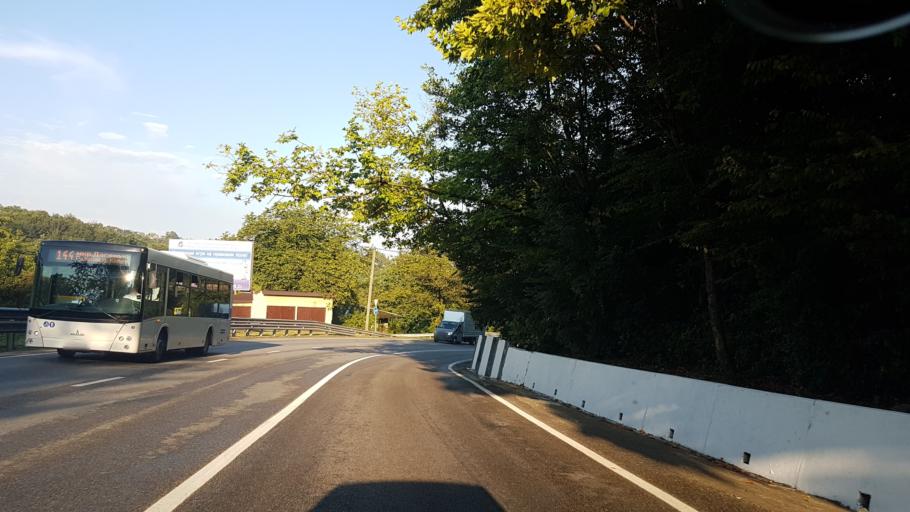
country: RU
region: Krasnodarskiy
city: Dagomys
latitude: 43.6622
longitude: 39.6813
